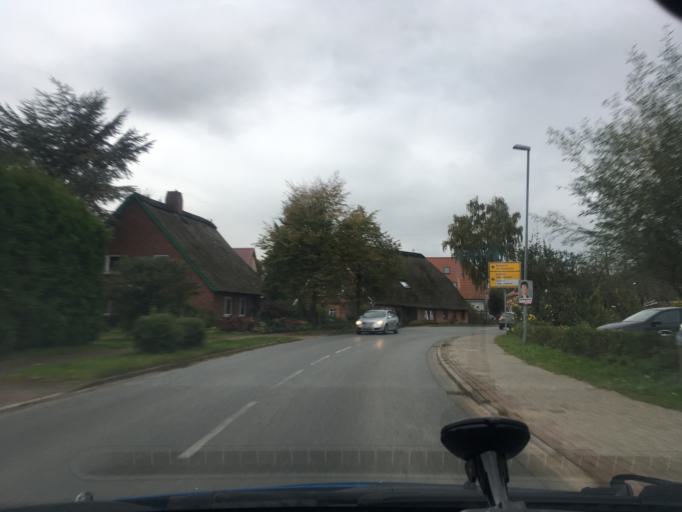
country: DE
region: Lower Saxony
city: Marschacht
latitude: 53.4164
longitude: 10.3704
